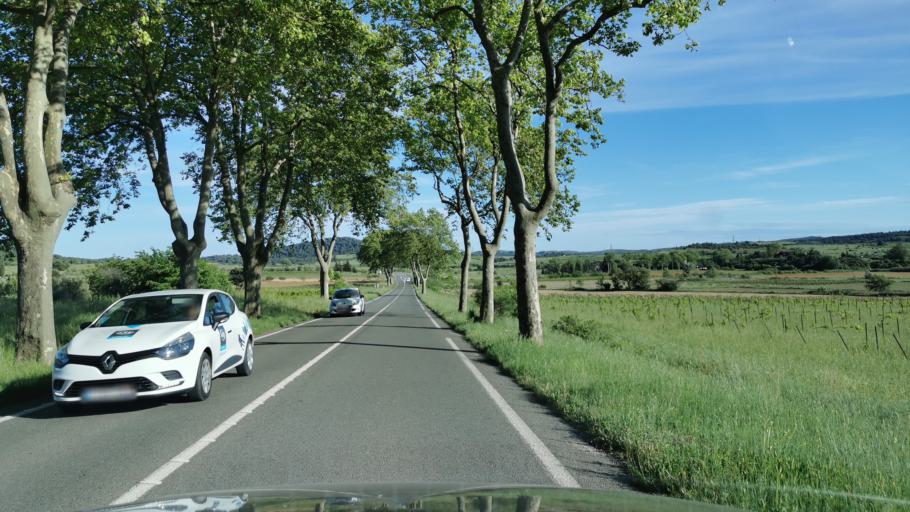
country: FR
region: Languedoc-Roussillon
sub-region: Departement de l'Aude
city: Marcorignan
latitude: 43.2209
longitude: 2.9257
